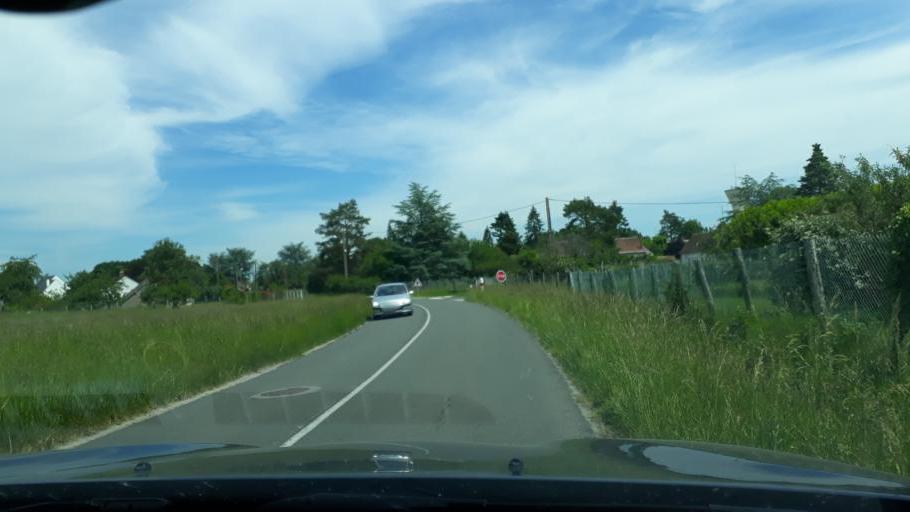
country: FR
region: Centre
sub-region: Departement du Loiret
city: Boiscommun
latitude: 48.0281
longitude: 2.3104
